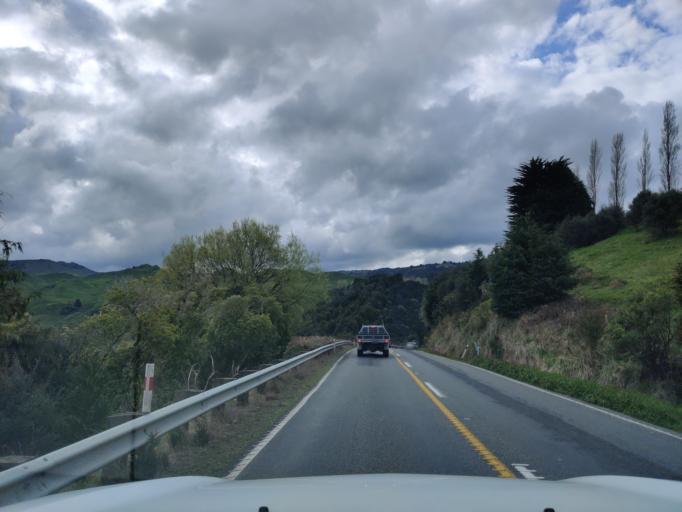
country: NZ
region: Manawatu-Wanganui
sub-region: Ruapehu District
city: Waiouru
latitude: -39.5039
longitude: 175.2886
